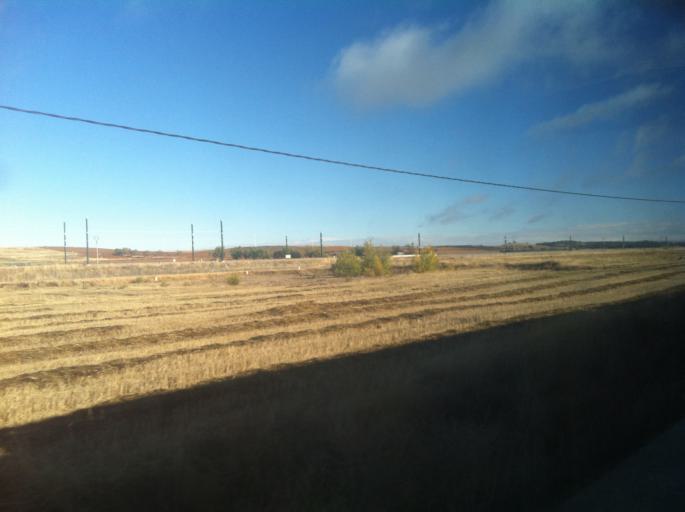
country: ES
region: Castille and Leon
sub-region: Provincia de Palencia
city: Villodrigo
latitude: 42.1438
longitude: -4.1119
